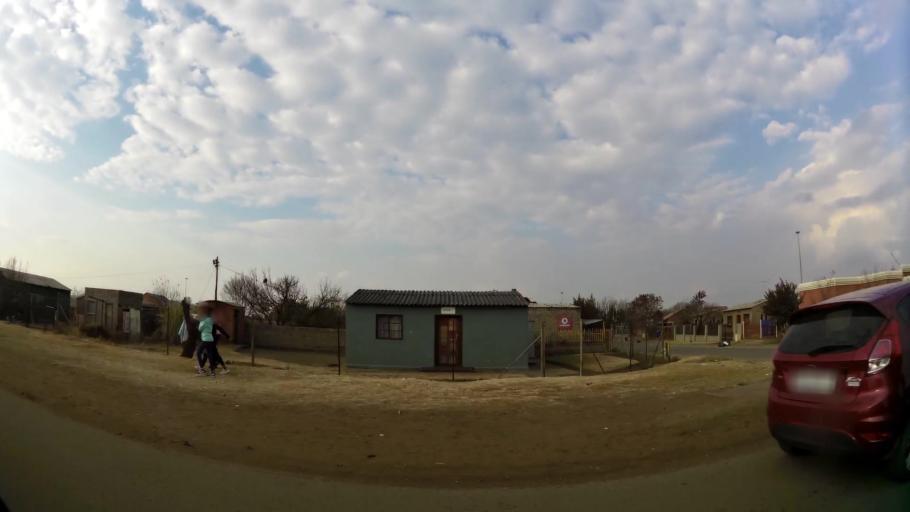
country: ZA
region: Gauteng
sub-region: Sedibeng District Municipality
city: Vanderbijlpark
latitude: -26.6792
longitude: 27.8756
